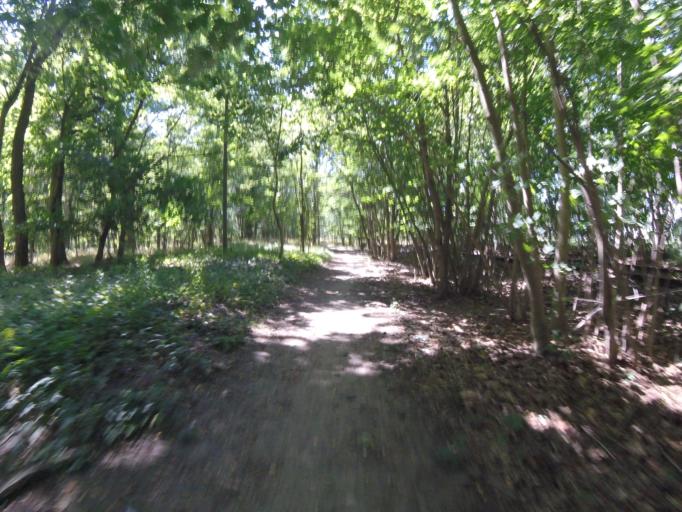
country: DE
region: Brandenburg
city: Konigs Wusterhausen
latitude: 52.2819
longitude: 13.6120
